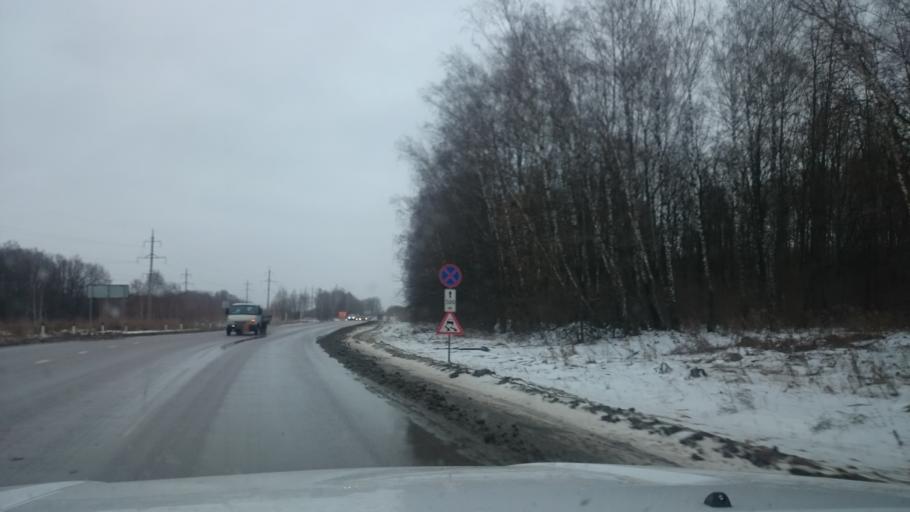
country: RU
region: Tula
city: Kosaya Gora
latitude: 54.1743
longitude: 37.4951
